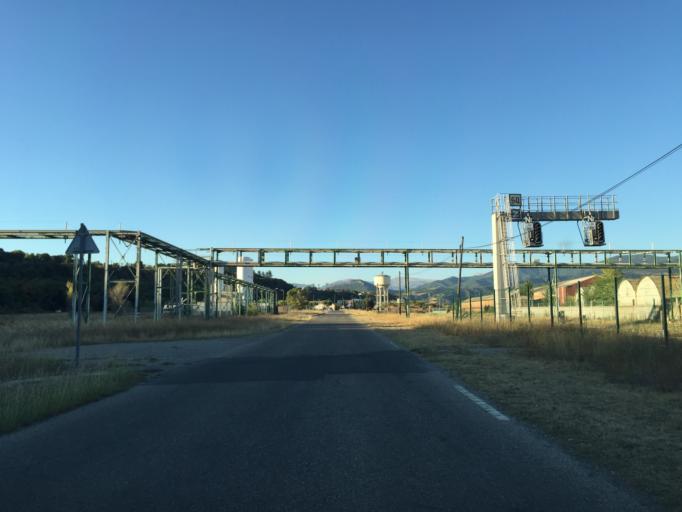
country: FR
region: Provence-Alpes-Cote d'Azur
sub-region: Departement des Alpes-de-Haute-Provence
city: Malijai
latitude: 44.0632
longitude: 5.9978
